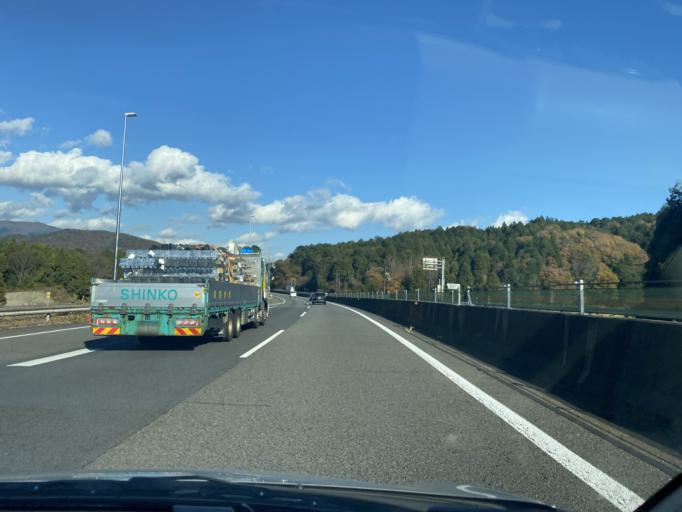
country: JP
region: Gifu
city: Tarui
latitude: 35.3340
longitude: 136.3998
